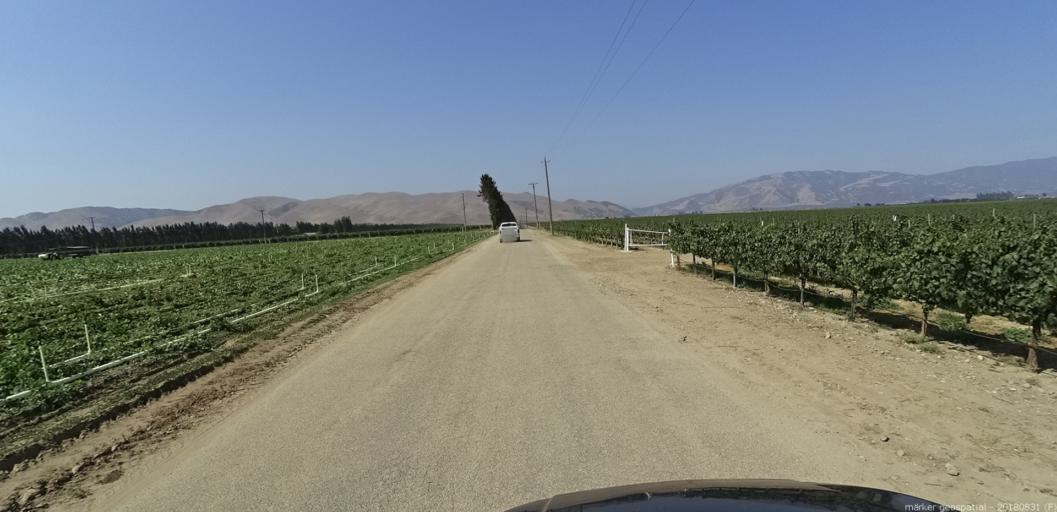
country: US
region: California
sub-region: Monterey County
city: Greenfield
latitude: 36.3059
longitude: -121.2335
